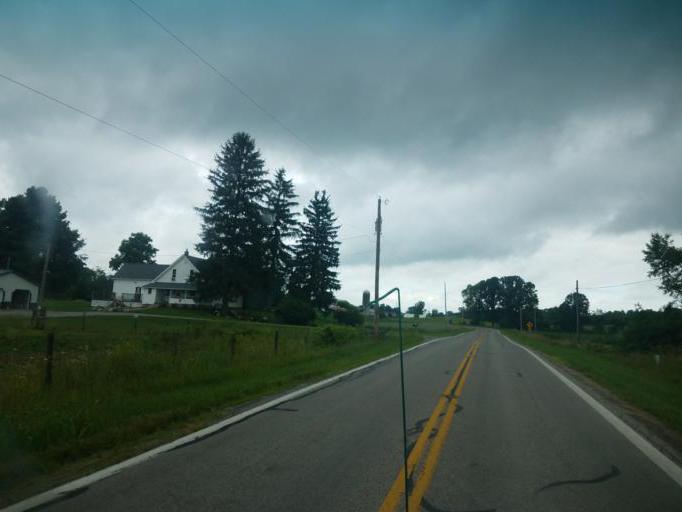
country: US
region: Ohio
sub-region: Logan County
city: Bellefontaine
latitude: 40.3760
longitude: -83.6744
